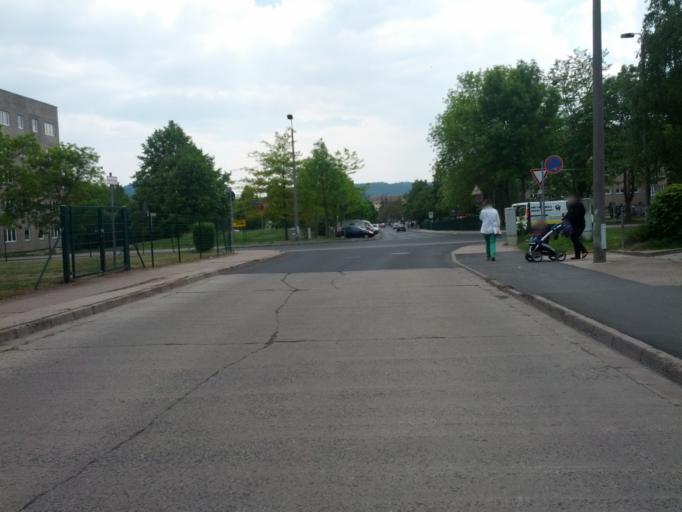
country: DE
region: Thuringia
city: Eisenach
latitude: 50.9968
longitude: 10.3122
